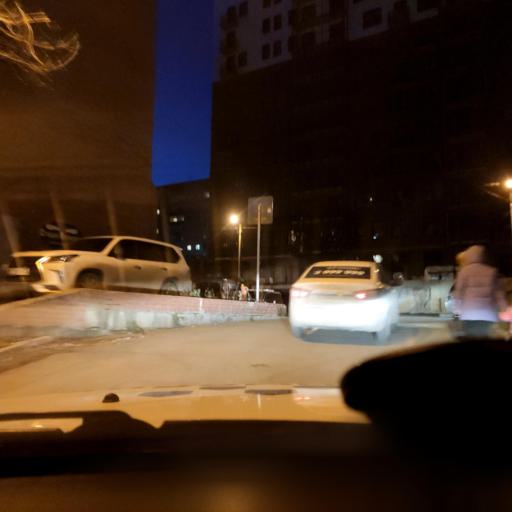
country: RU
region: Perm
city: Perm
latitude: 58.0087
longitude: 56.2072
